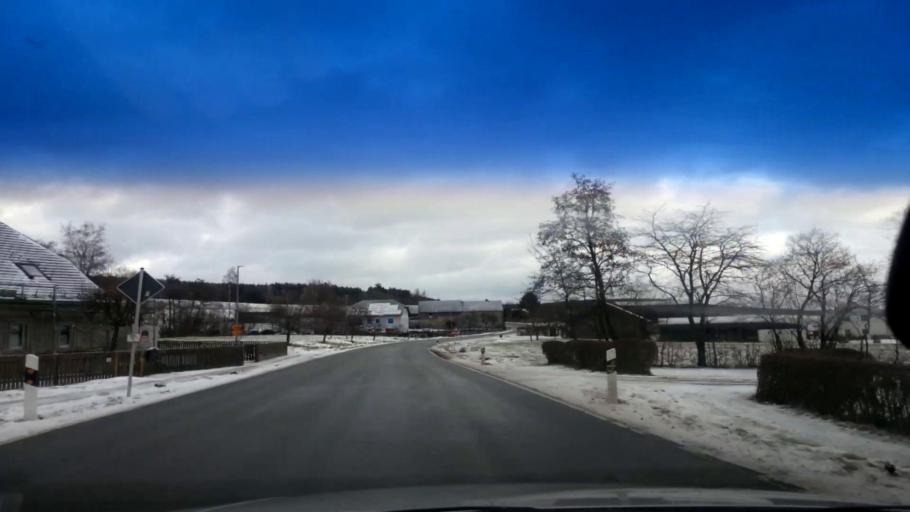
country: DE
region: Bavaria
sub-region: Upper Franconia
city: Grub
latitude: 50.1283
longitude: 11.9209
